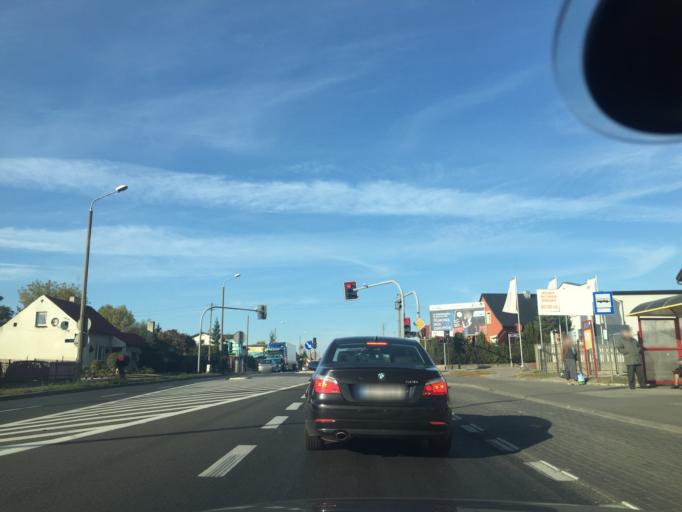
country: PL
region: Kujawsko-Pomorskie
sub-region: Powiat inowroclawski
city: Inowroclaw
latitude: 52.7615
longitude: 18.2573
